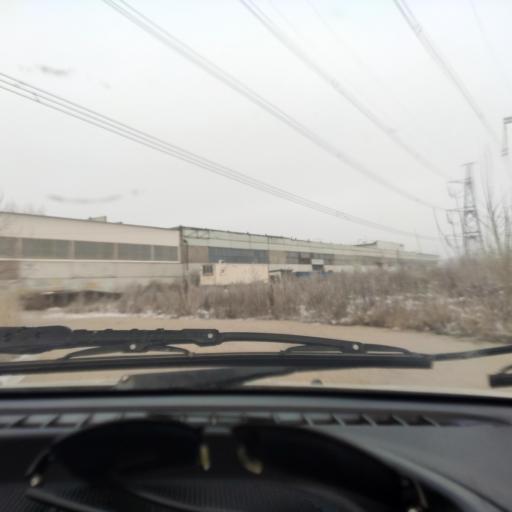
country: RU
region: Samara
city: Zhigulevsk
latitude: 53.4760
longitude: 49.5056
